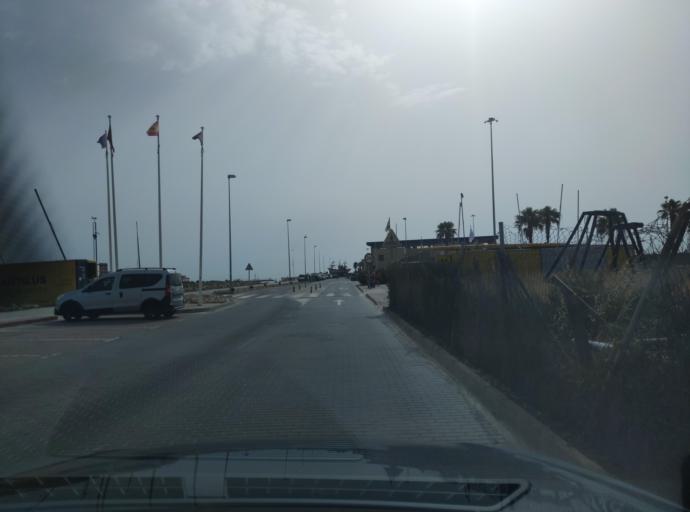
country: ES
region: Valencia
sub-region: Provincia de Alicante
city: Guardamar del Segura
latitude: 38.1096
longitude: -0.6477
